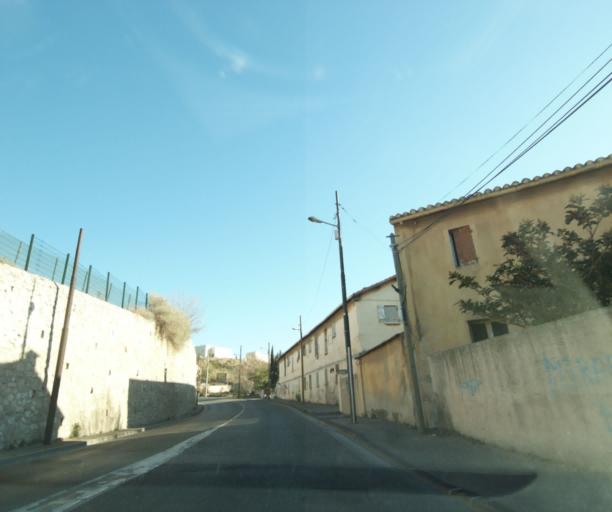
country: FR
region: Provence-Alpes-Cote d'Azur
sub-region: Departement des Bouches-du-Rhone
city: Marseille 16
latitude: 43.3544
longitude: 5.3513
